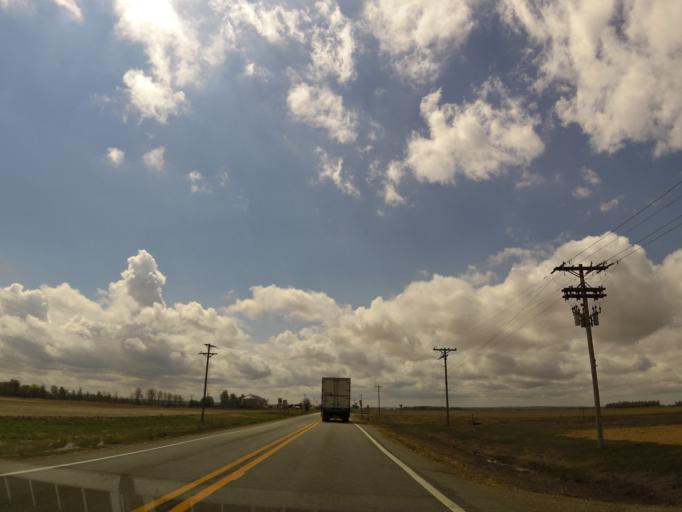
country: US
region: Arkansas
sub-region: Clay County
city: Corning
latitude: 36.3205
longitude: -90.5252
